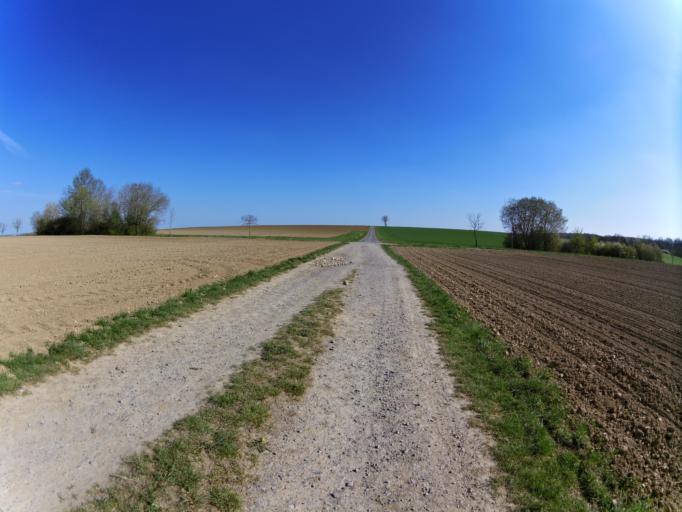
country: DE
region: Bavaria
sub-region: Regierungsbezirk Unterfranken
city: Kurnach
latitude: 49.8649
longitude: 10.0084
